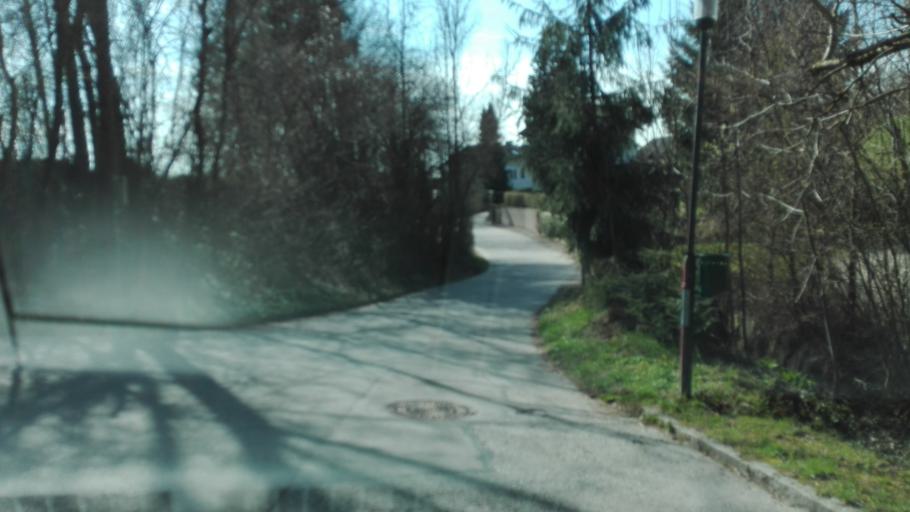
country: AT
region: Lower Austria
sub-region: Politischer Bezirk Amstetten
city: Ennsdorf
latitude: 48.2480
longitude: 14.5087
